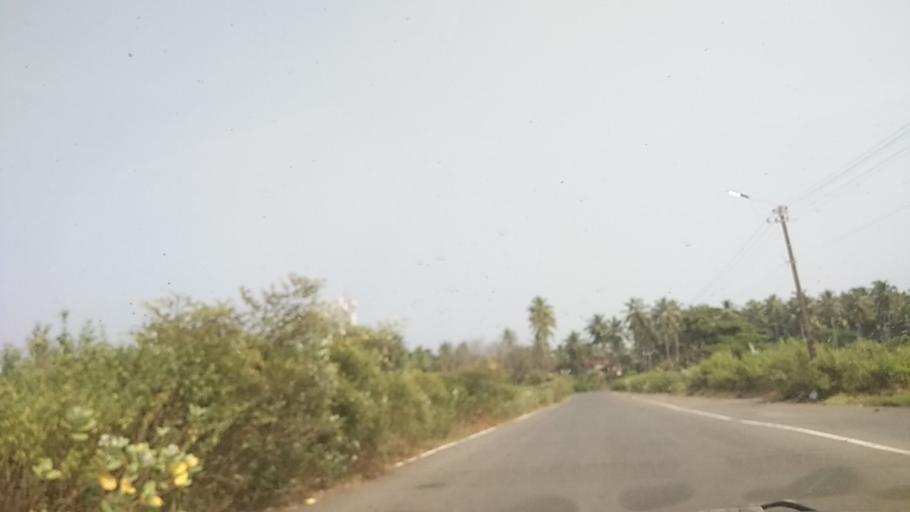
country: IN
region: Goa
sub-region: South Goa
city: Cuncolim
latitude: 15.1651
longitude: 73.9700
